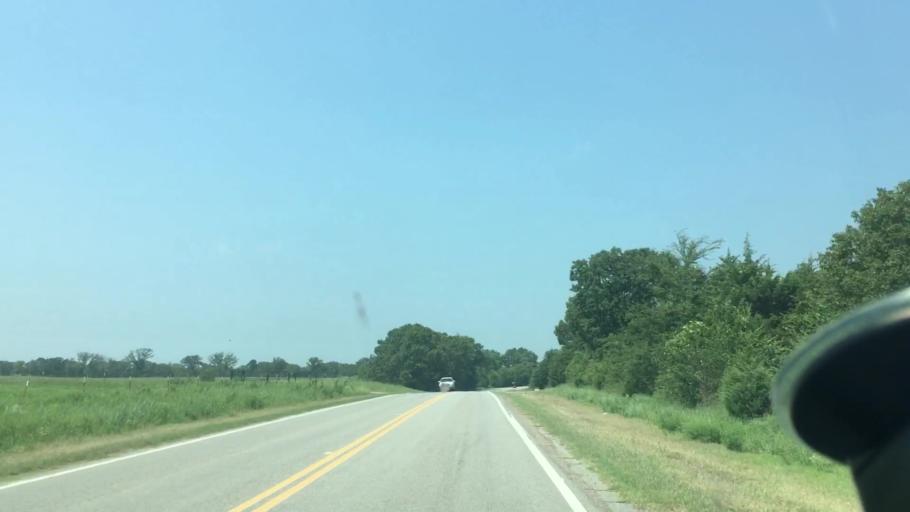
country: US
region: Oklahoma
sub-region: Atoka County
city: Atoka
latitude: 34.2799
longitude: -95.9460
